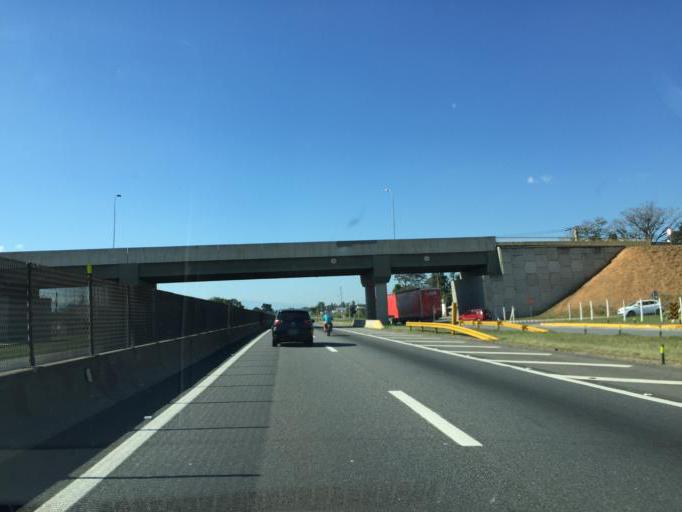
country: BR
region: Sao Paulo
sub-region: Lorena
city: Lorena
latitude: -22.7814
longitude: -45.1475
